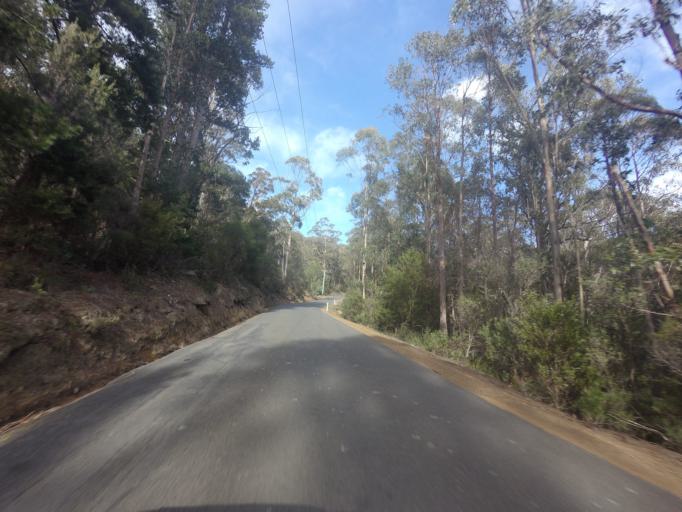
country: AU
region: Tasmania
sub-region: Kingborough
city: Margate
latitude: -43.0048
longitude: 147.1705
